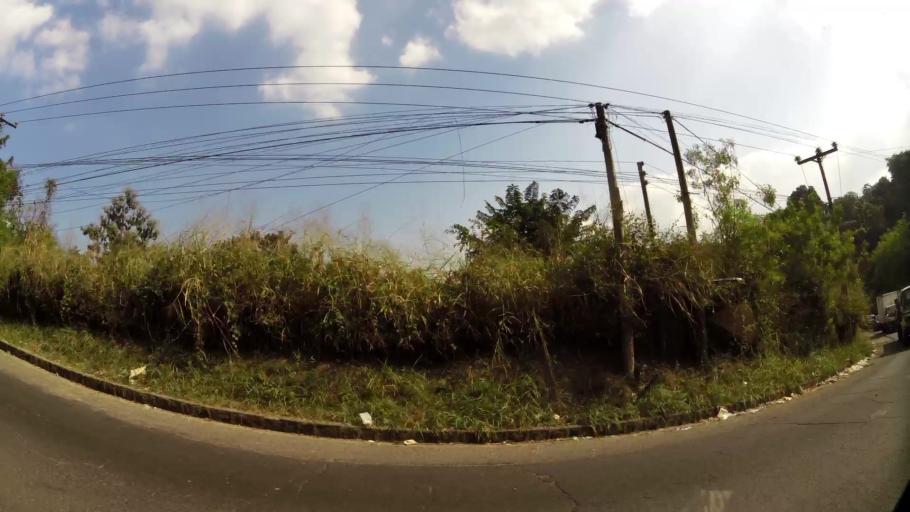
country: SV
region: San Salvador
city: Delgado
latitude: 13.7179
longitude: -89.1625
